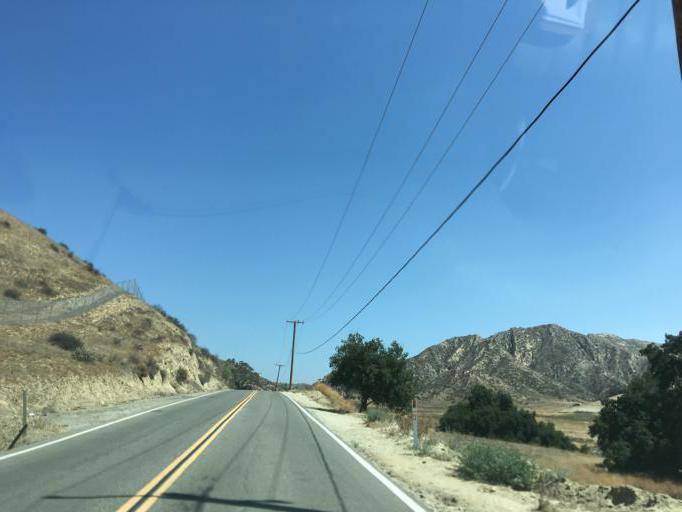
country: US
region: California
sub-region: Los Angeles County
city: Val Verde
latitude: 34.4291
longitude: -118.6587
